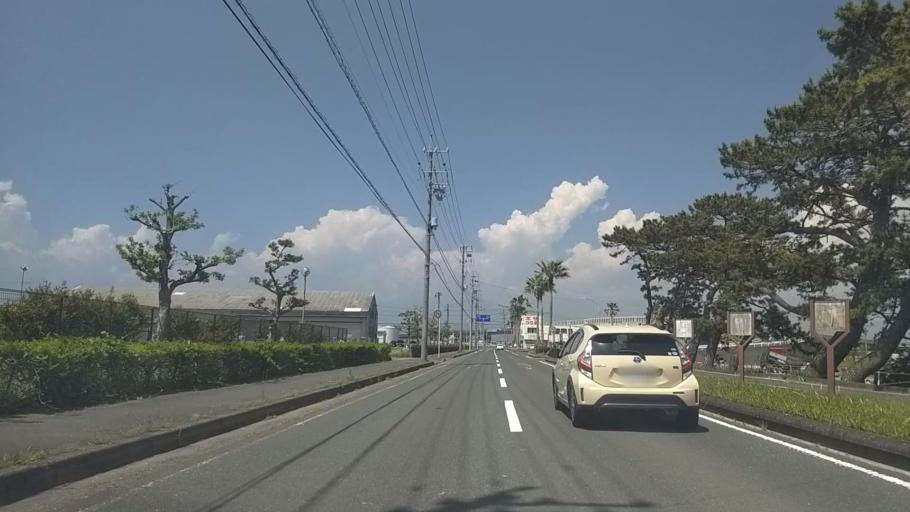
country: JP
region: Shizuoka
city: Kosai-shi
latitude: 34.6921
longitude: 137.5779
